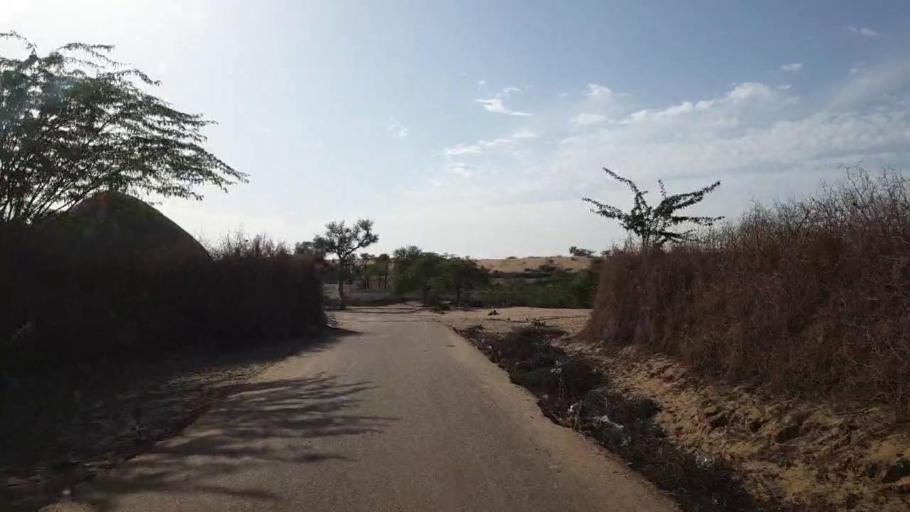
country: PK
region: Sindh
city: Nabisar
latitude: 25.0435
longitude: 70.0092
